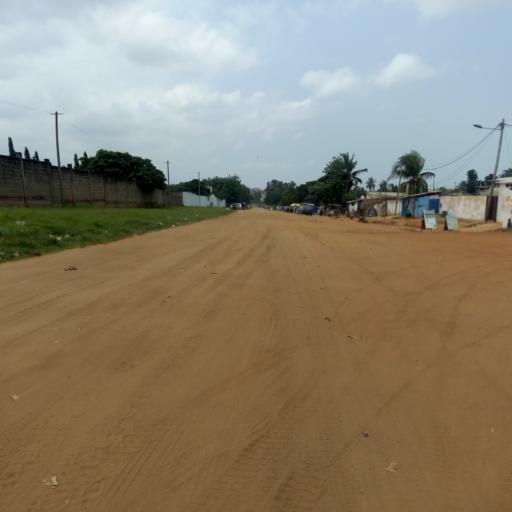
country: TG
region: Maritime
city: Lome
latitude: 6.1866
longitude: 1.1705
